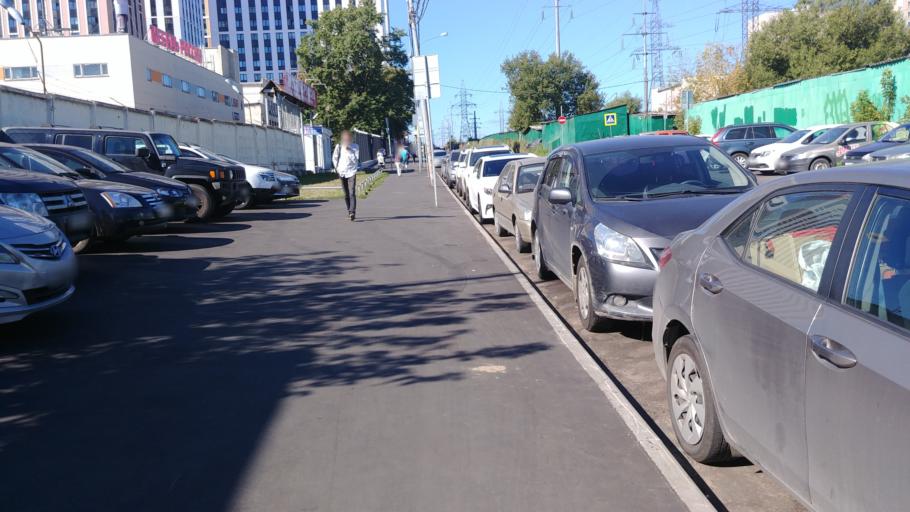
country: RU
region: Moscow
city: Golovinskiy
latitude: 55.8424
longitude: 37.4976
